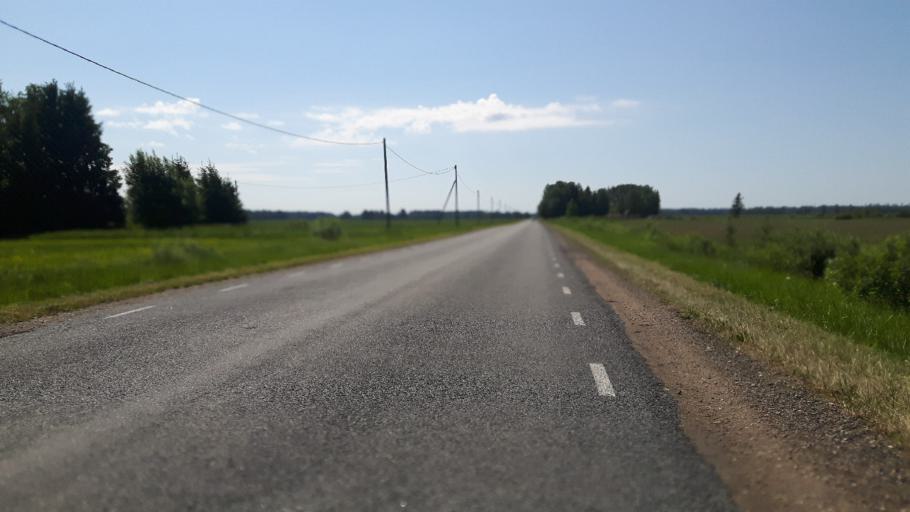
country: EE
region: Paernumaa
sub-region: Vaendra vald (alev)
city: Vandra
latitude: 58.6247
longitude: 25.0210
